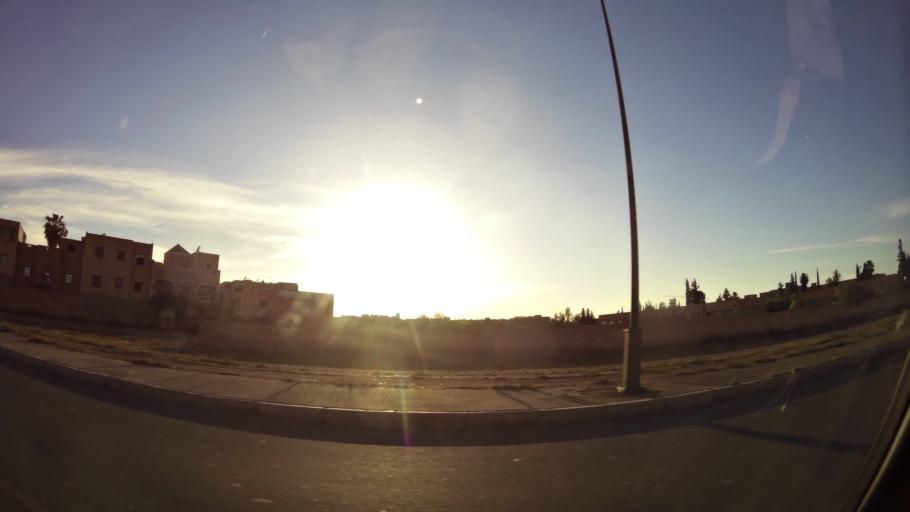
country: MA
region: Marrakech-Tensift-Al Haouz
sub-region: Marrakech
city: Marrakesh
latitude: 31.6207
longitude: -8.0442
